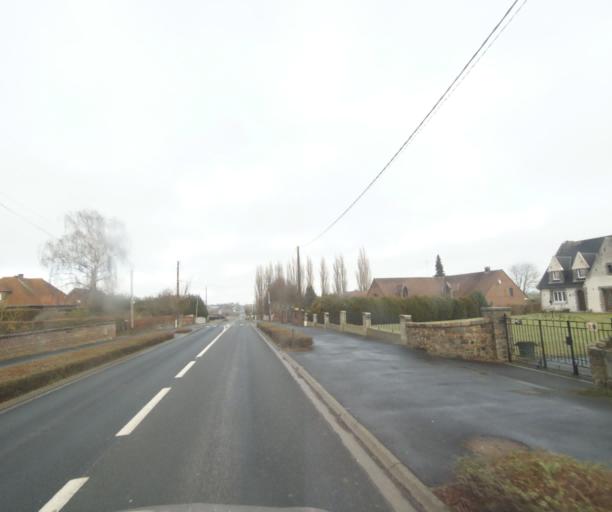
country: FR
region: Nord-Pas-de-Calais
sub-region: Departement du Nord
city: Famars
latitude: 50.2932
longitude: 3.5146
